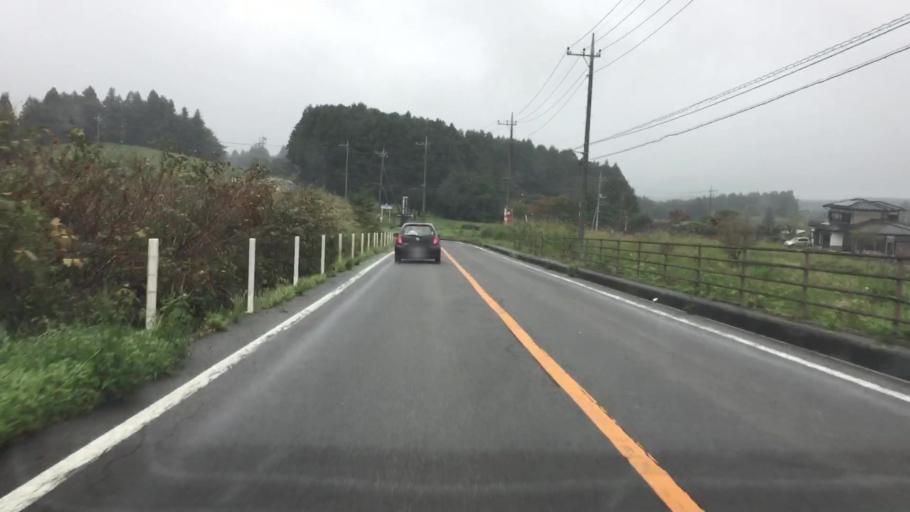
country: JP
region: Yamanashi
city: Fujikawaguchiko
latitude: 35.4033
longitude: 138.6134
